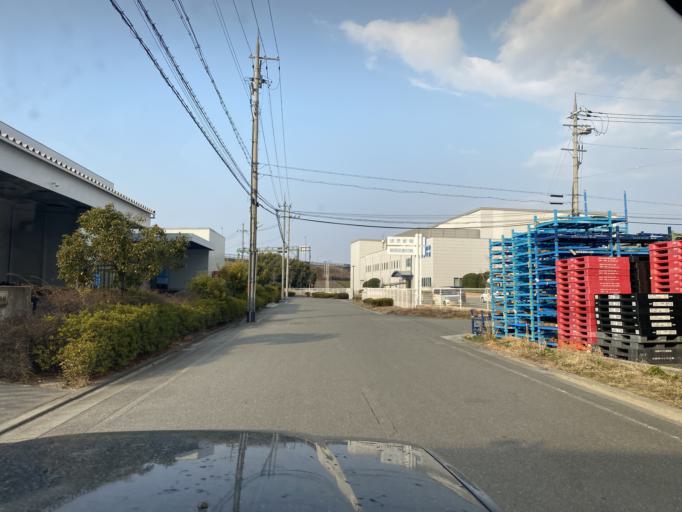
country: JP
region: Kyoto
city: Yawata
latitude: 34.8673
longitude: 135.7411
